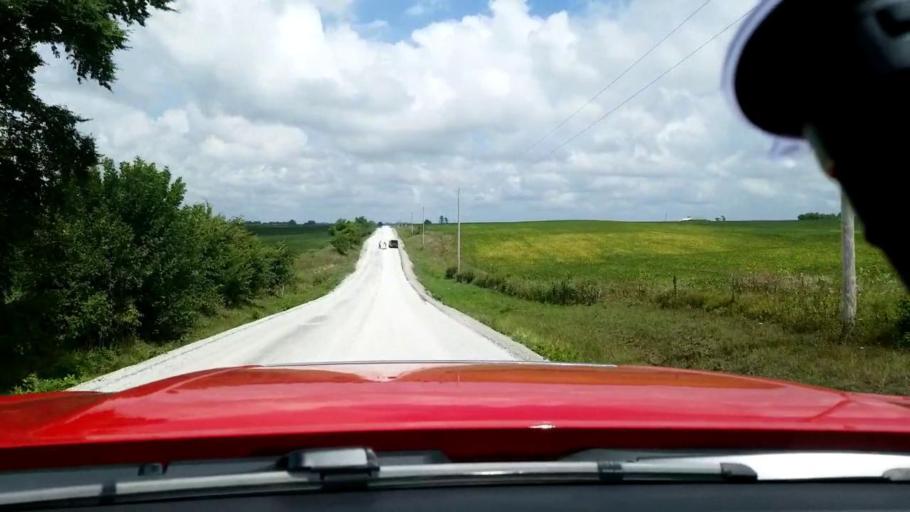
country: US
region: Iowa
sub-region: Decatur County
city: Lamoni
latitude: 40.6622
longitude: -94.0483
